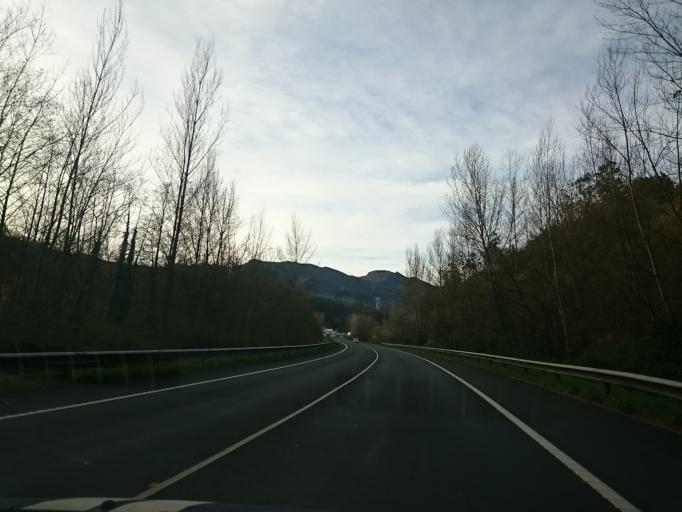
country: ES
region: Asturias
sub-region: Province of Asturias
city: Oviedo
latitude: 43.3083
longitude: -5.8245
